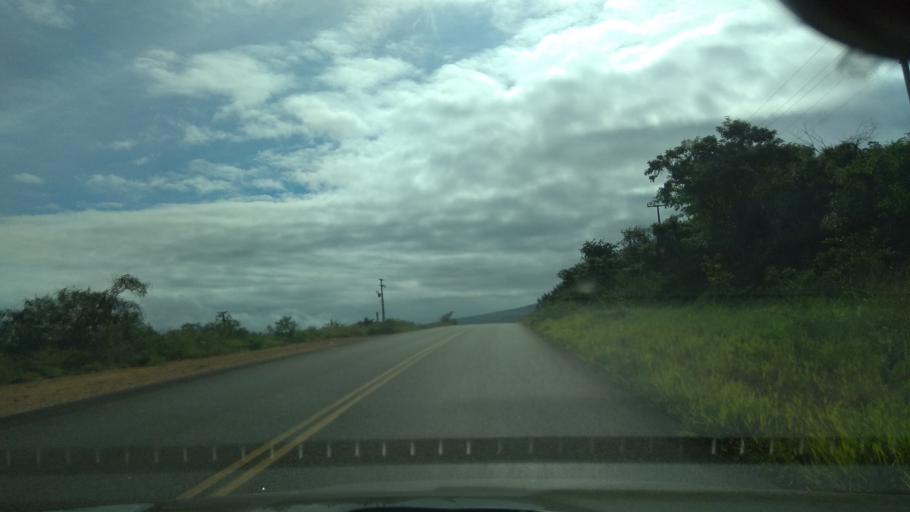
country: BR
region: Bahia
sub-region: Santa Ines
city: Santa Ines
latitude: -13.3545
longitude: -39.8788
